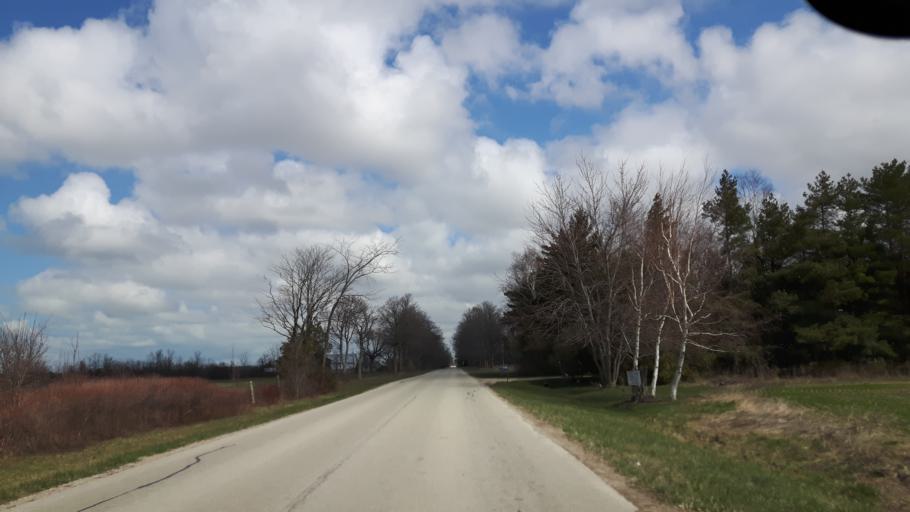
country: CA
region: Ontario
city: Goderich
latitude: 43.6515
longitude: -81.6846
